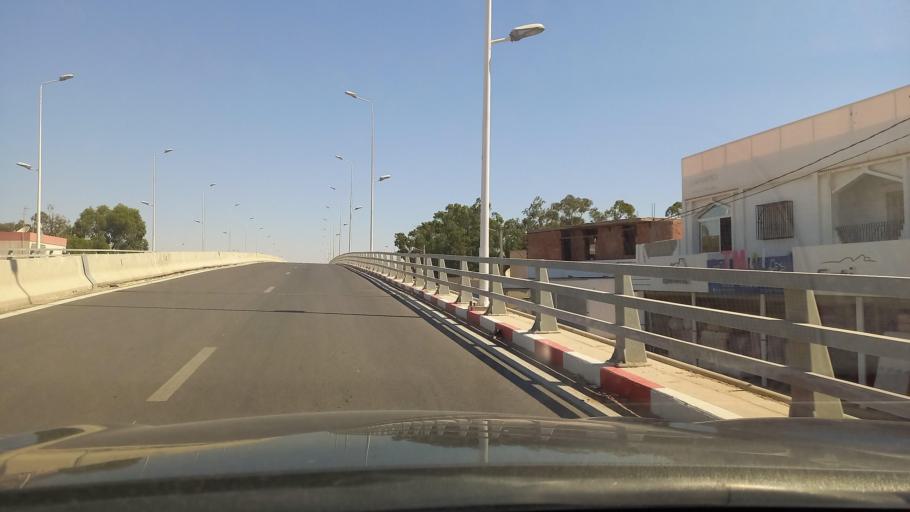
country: TN
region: Safaqis
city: Sfax
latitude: 34.7321
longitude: 10.7248
